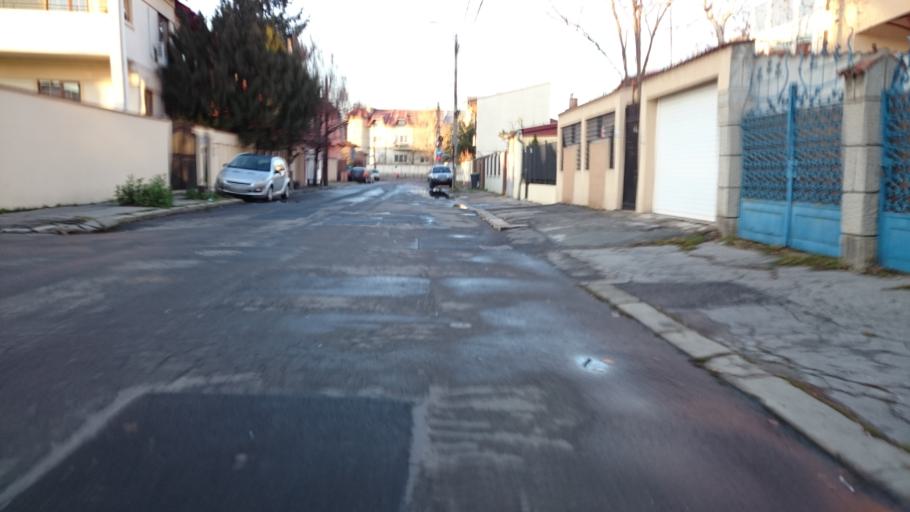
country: RO
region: Bucuresti
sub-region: Municipiul Bucuresti
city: Bucuresti
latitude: 44.4202
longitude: 26.0579
